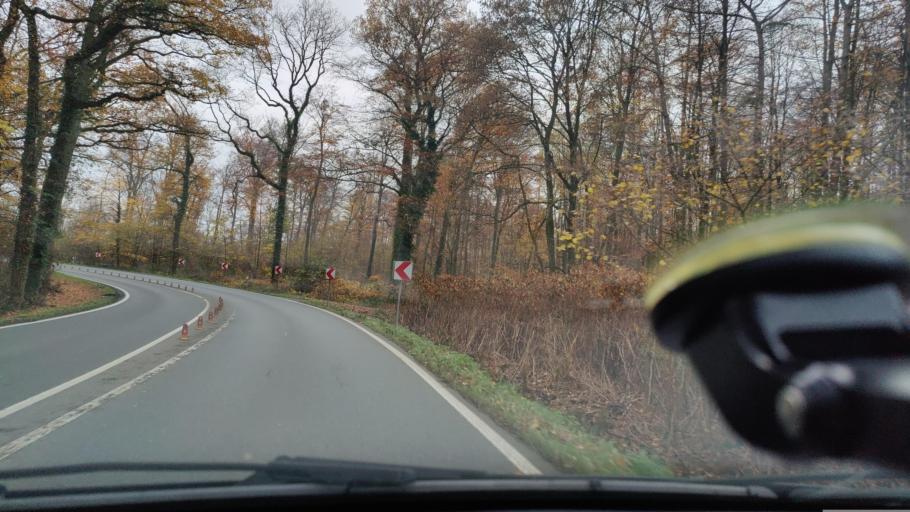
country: DE
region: North Rhine-Westphalia
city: Lunen
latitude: 51.6458
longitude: 7.5060
